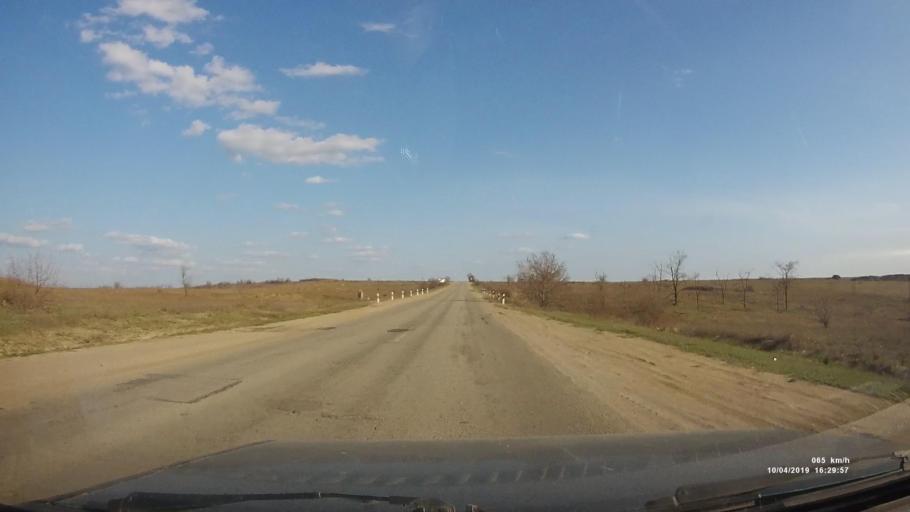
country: RU
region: Rostov
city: Staraya Stanitsa
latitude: 48.2653
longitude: 40.3608
